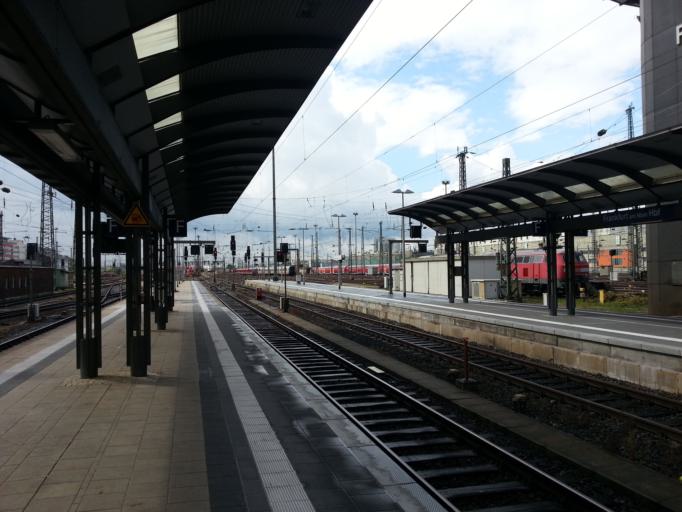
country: DE
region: Hesse
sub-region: Regierungsbezirk Darmstadt
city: Frankfurt am Main
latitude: 50.1050
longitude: 8.6594
